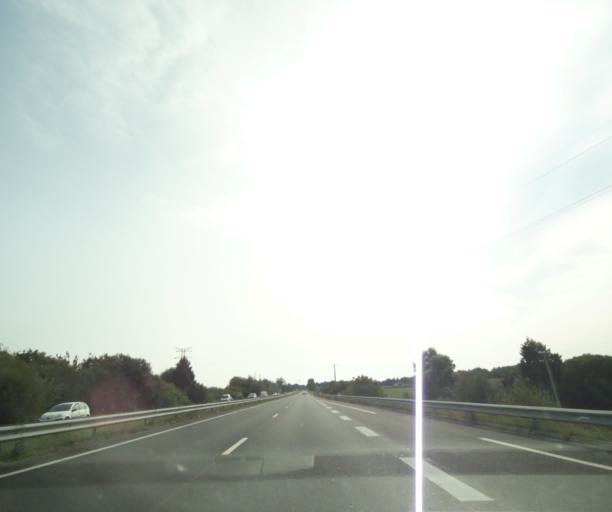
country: FR
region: Brittany
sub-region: Departement des Cotes-d'Armor
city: Quevert
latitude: 48.4669
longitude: -2.0661
